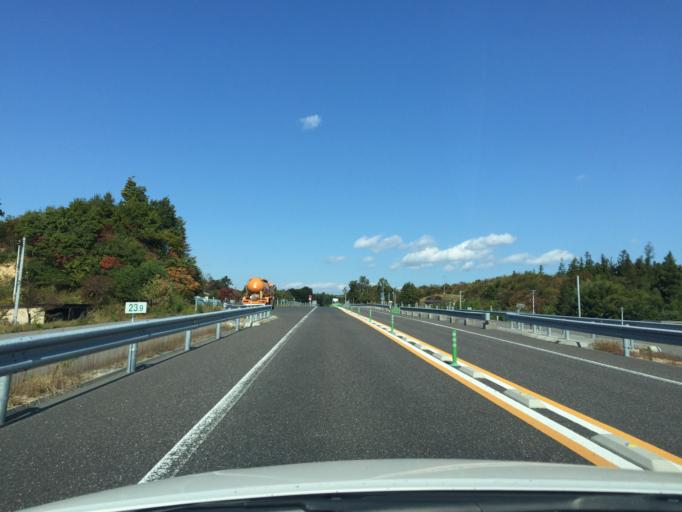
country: JP
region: Fukushima
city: Ishikawa
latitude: 37.2206
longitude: 140.5437
